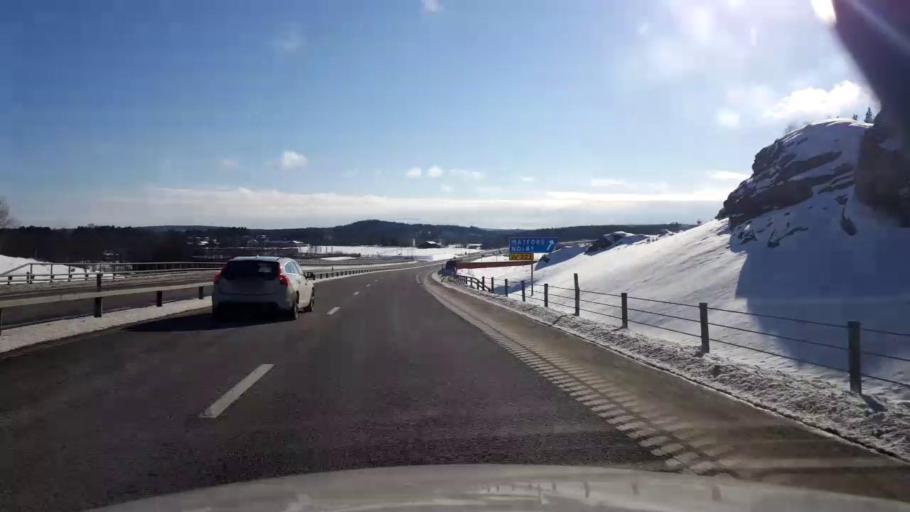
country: SE
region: Vaesternorrland
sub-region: Sundsvalls Kommun
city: Nolby
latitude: 62.2987
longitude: 17.3474
